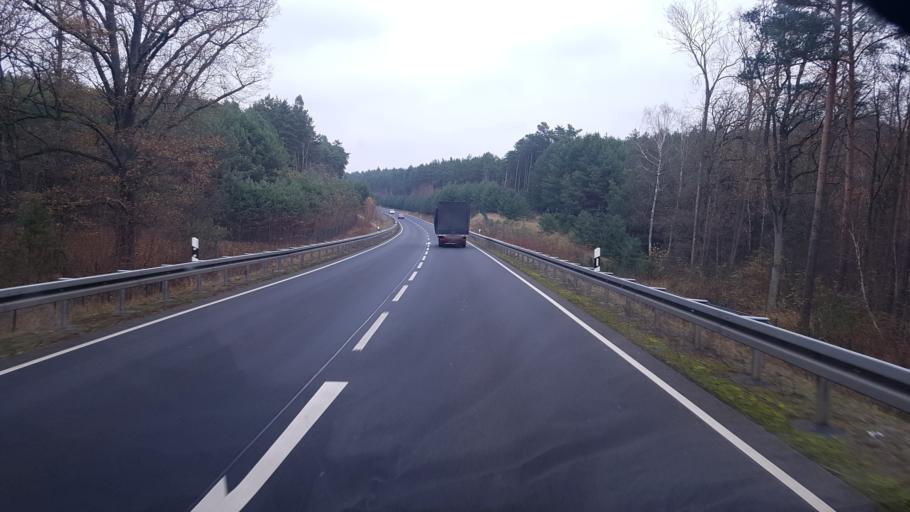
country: DE
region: Brandenburg
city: Schenkendobern
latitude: 51.9807
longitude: 14.6530
